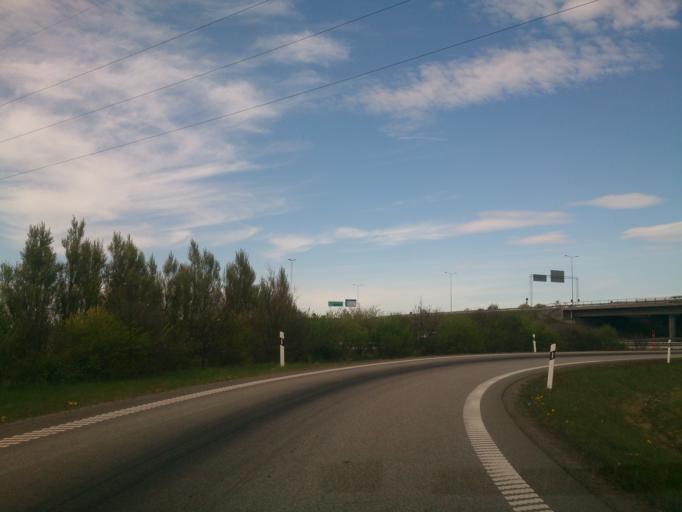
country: SE
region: OEstergoetland
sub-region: Linkopings Kommun
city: Linkoping
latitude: 58.4376
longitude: 15.5801
